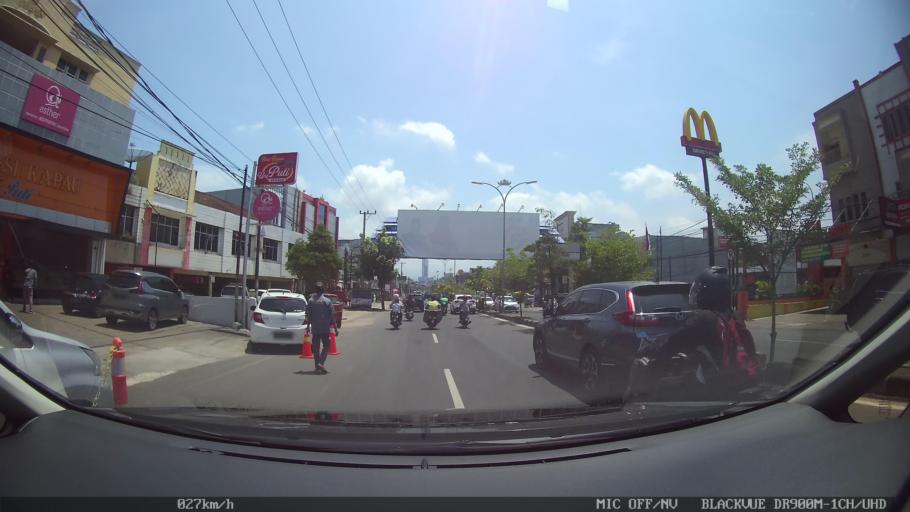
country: ID
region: Lampung
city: Bandarlampung
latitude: -5.4054
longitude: 105.2775
